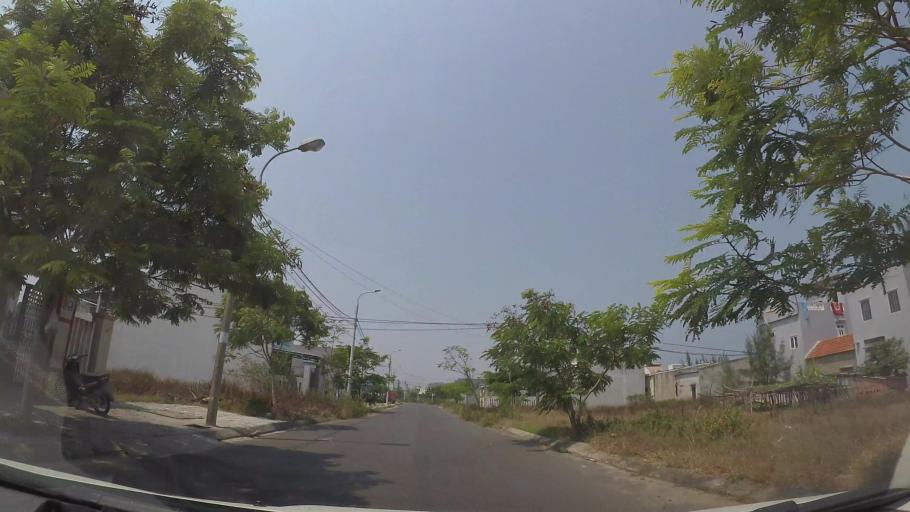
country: VN
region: Da Nang
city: Ngu Hanh Son
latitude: 15.9895
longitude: 108.2683
